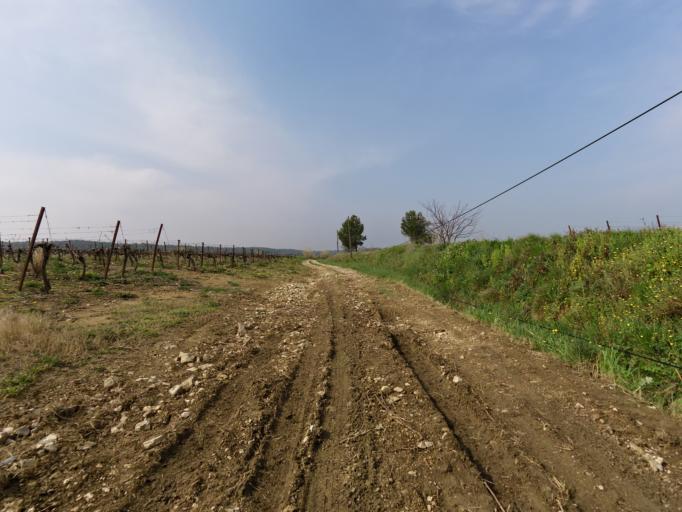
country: FR
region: Languedoc-Roussillon
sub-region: Departement du Gard
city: Calvisson
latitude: 43.7721
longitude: 4.1958
